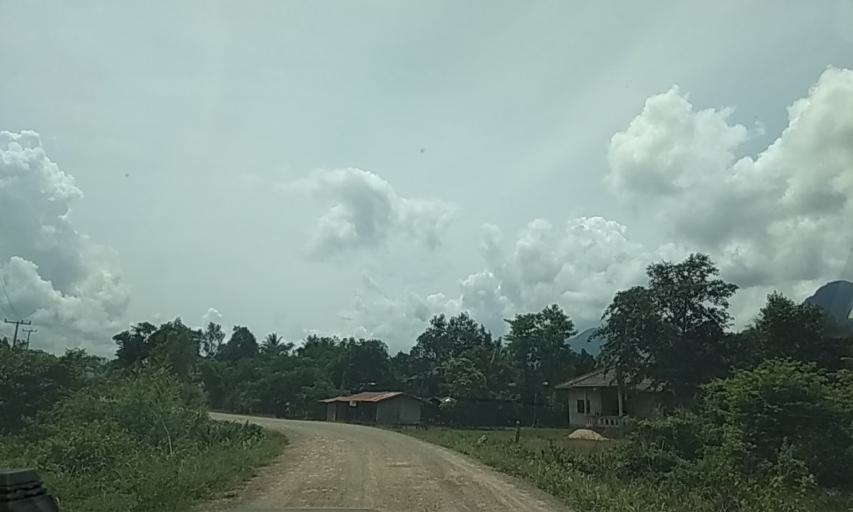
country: LA
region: Bolikhamxai
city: Ban Nahin
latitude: 18.1522
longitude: 104.7242
